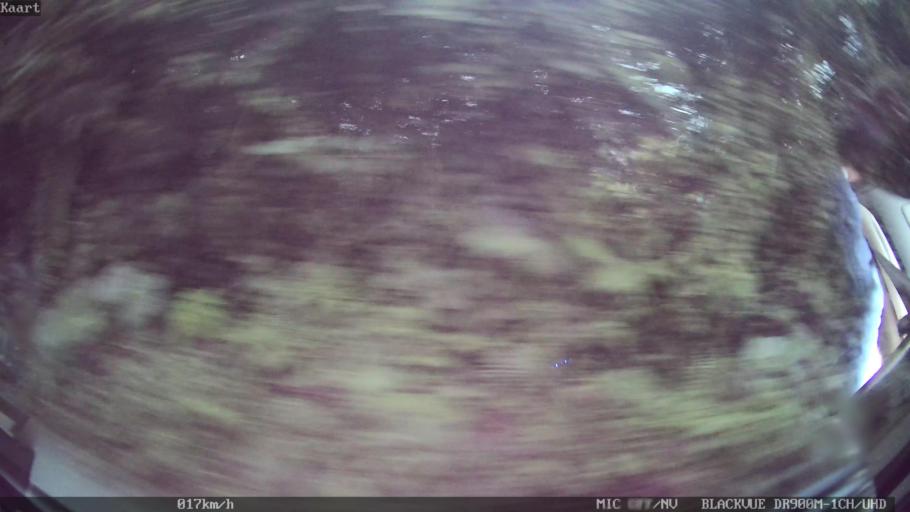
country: ID
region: Bali
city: Peneng
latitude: -8.3240
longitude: 115.1871
